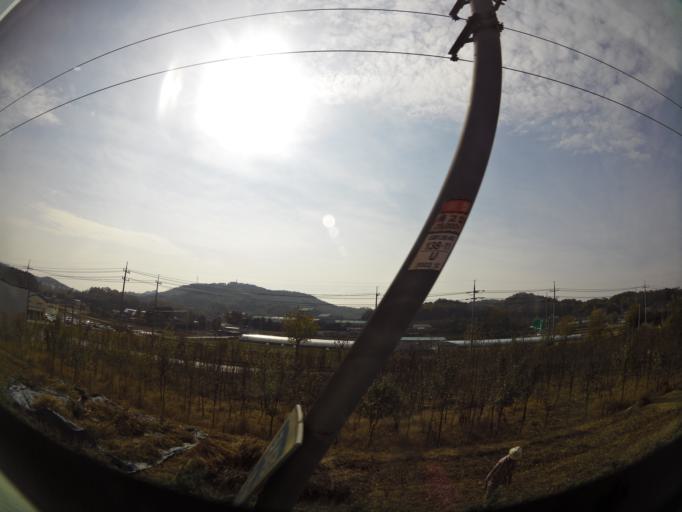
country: KR
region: Daejeon
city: Songgang-dong
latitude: 36.5365
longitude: 127.3464
